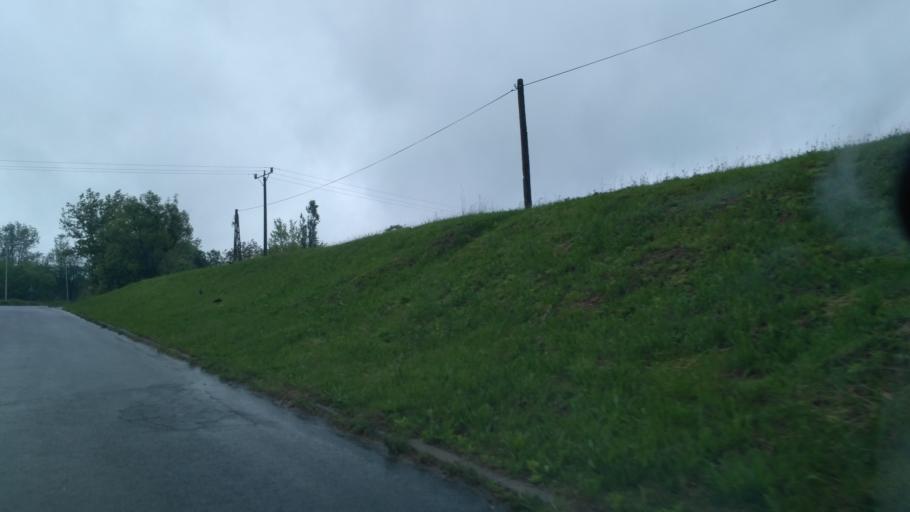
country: PL
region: Subcarpathian Voivodeship
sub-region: Powiat jasielski
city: Jaslo
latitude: 49.7559
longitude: 21.4842
